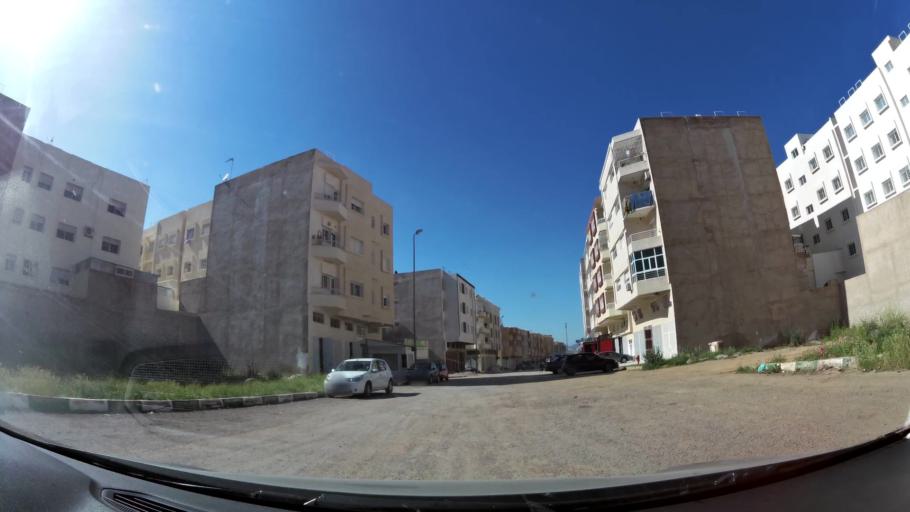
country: MA
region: Fes-Boulemane
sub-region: Fes
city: Fes
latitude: 33.9981
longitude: -5.0045
